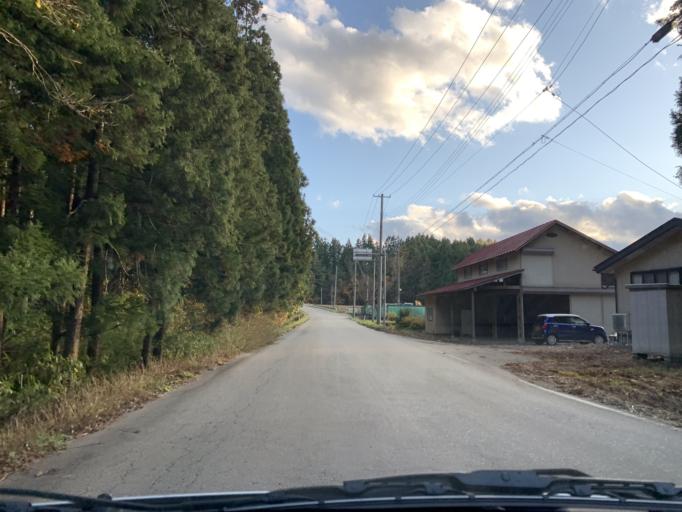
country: JP
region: Iwate
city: Mizusawa
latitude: 39.1196
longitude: 141.0368
